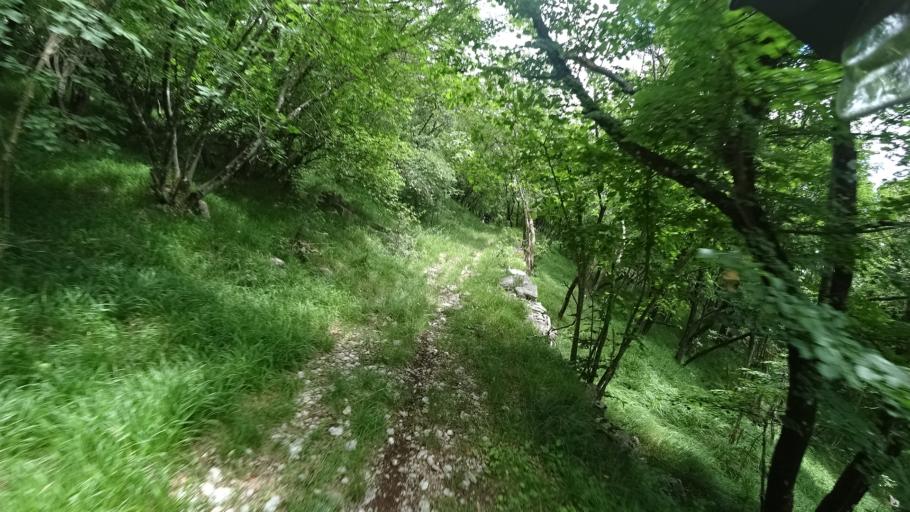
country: HR
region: Primorsko-Goranska
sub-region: Grad Crikvenica
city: Crikvenica
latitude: 45.2207
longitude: 14.7388
